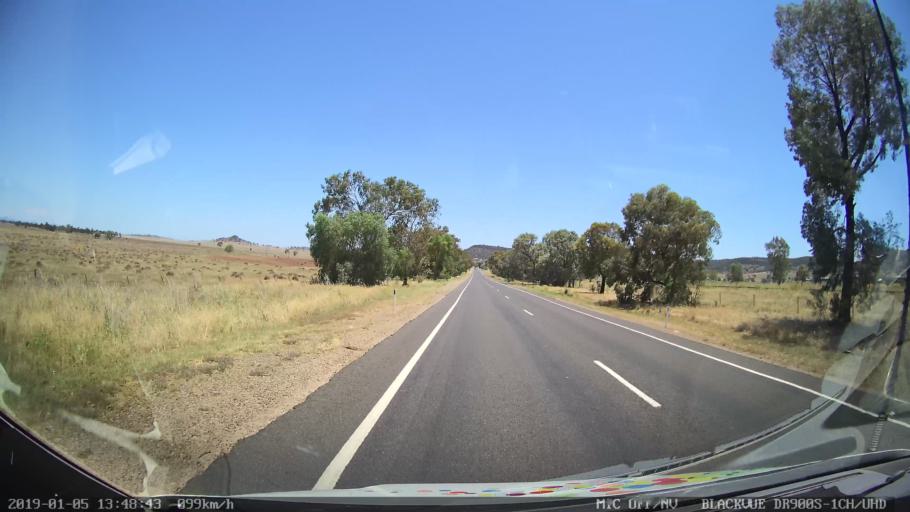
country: AU
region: New South Wales
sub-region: Gunnedah
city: Gunnedah
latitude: -31.0057
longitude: 150.2766
